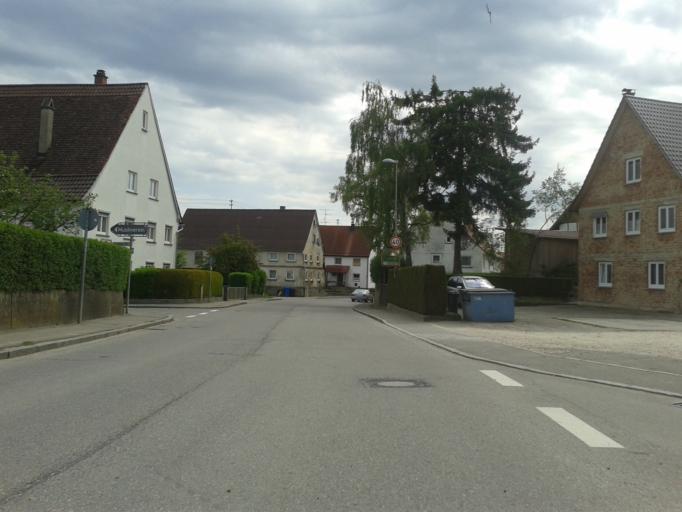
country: DE
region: Baden-Wuerttemberg
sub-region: Tuebingen Region
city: Erbach
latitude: 48.3530
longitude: 9.8966
